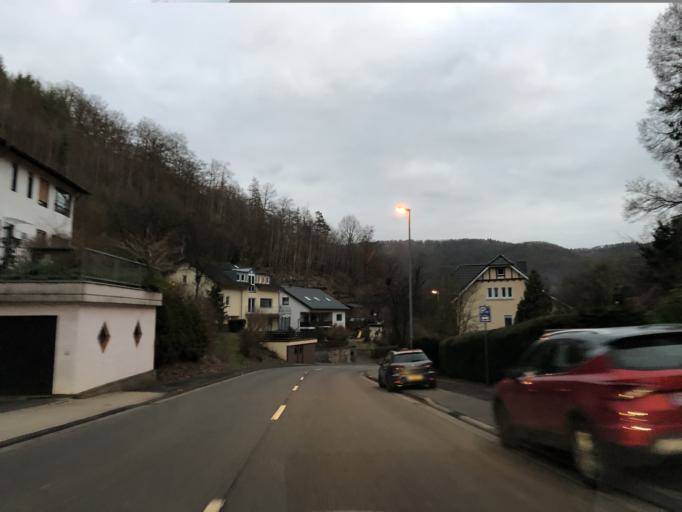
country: DE
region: Rheinland-Pfalz
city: Bad Ems
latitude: 50.3398
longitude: 7.7056
